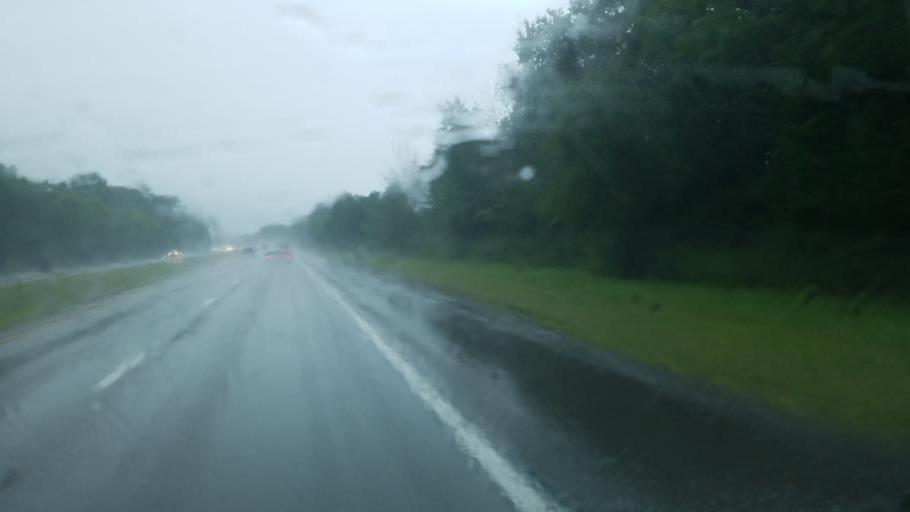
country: US
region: Ohio
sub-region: Trumbull County
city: Morgandale
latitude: 41.2624
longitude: -80.7703
